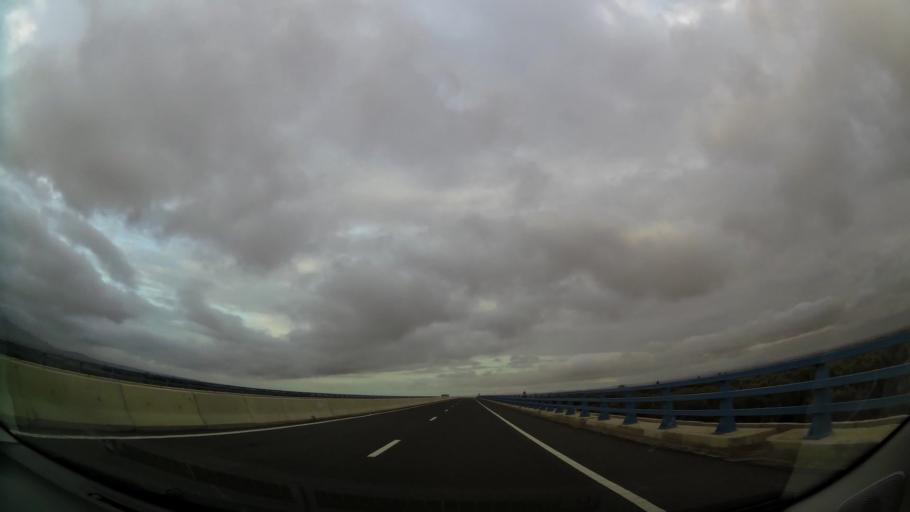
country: MA
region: Taza-Al Hoceima-Taounate
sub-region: Taza
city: Guercif
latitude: 34.3617
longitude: -3.2936
